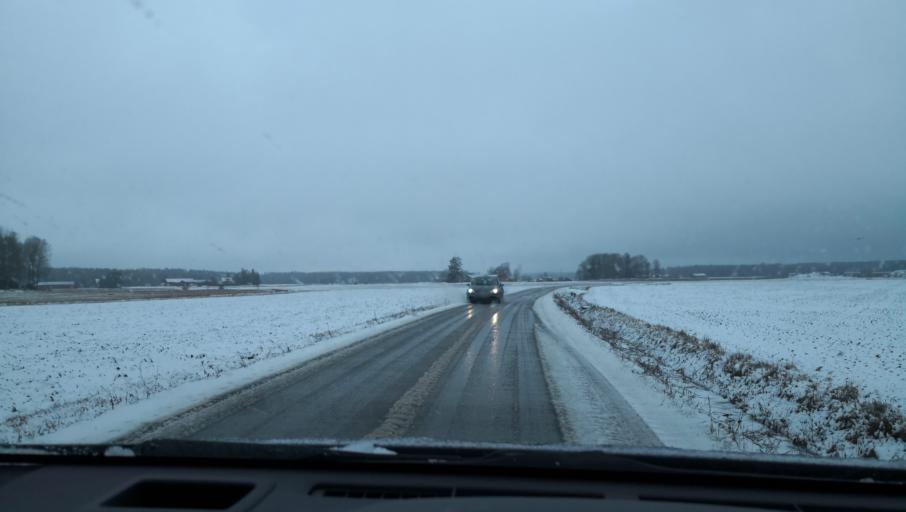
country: SE
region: Vaestmanland
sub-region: Hallstahammars Kommun
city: Hallstahammar
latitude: 59.5970
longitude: 16.1388
